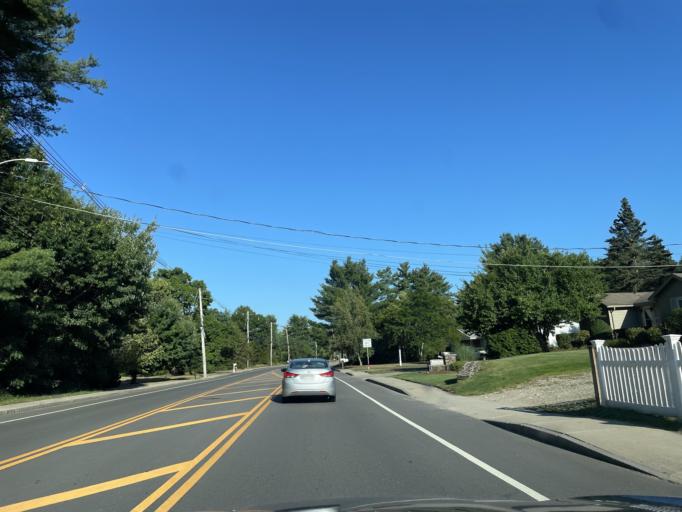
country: US
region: Massachusetts
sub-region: Bristol County
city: Mansfield
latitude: 42.0310
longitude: -71.1865
